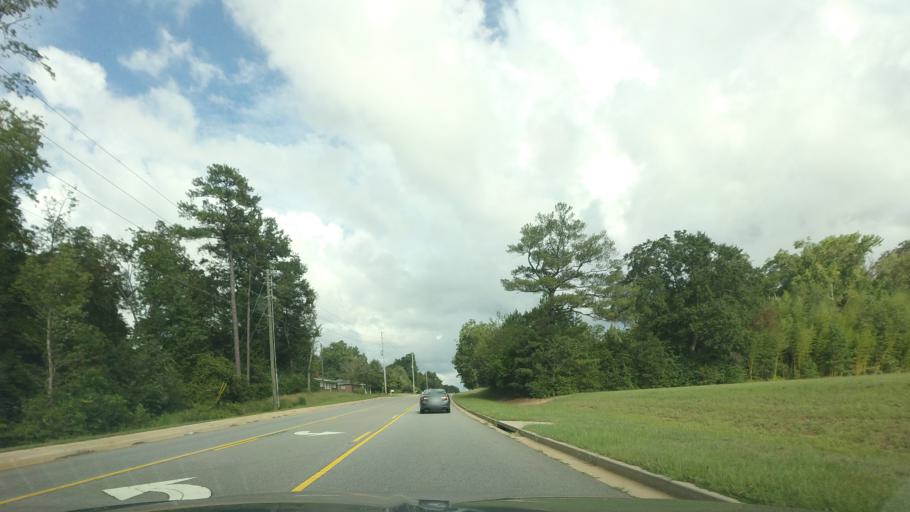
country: US
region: Georgia
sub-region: Houston County
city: Centerville
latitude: 32.6349
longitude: -83.7001
